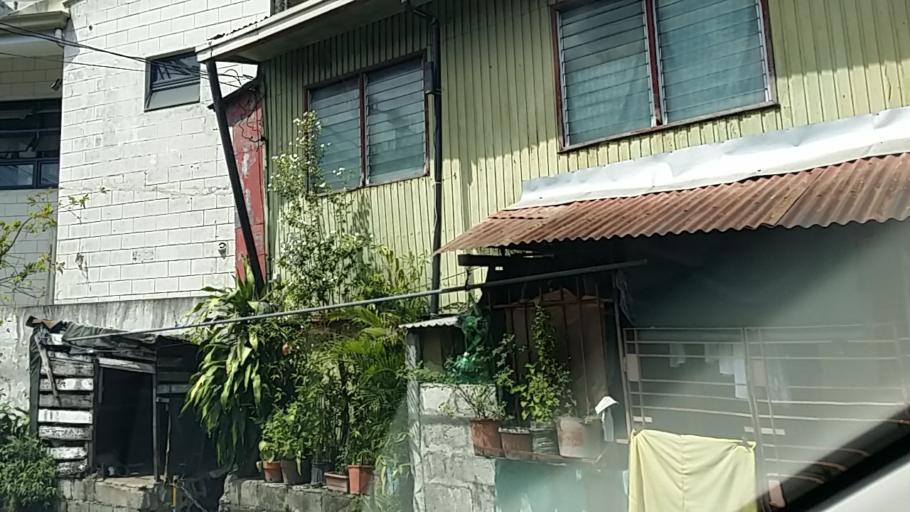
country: PH
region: Metro Manila
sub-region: Mandaluyong
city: Mandaluyong City
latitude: 14.5840
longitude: 121.0466
